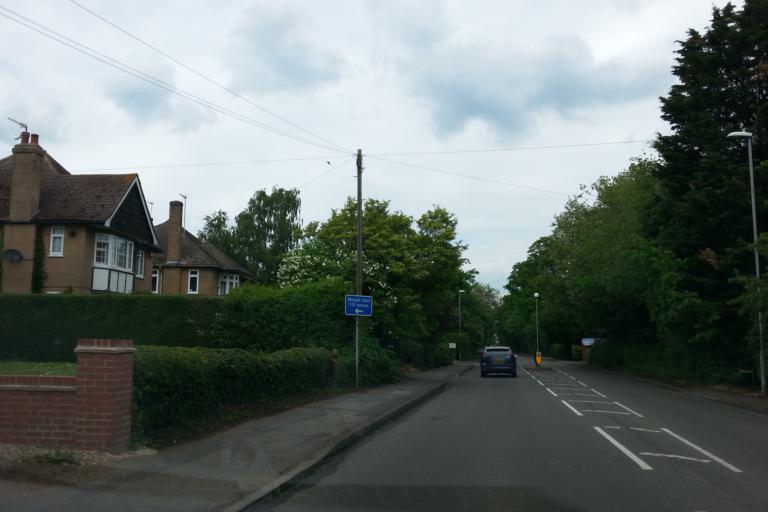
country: GB
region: England
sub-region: Cambridgeshire
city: Ramsey
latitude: 52.4437
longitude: -0.1125
